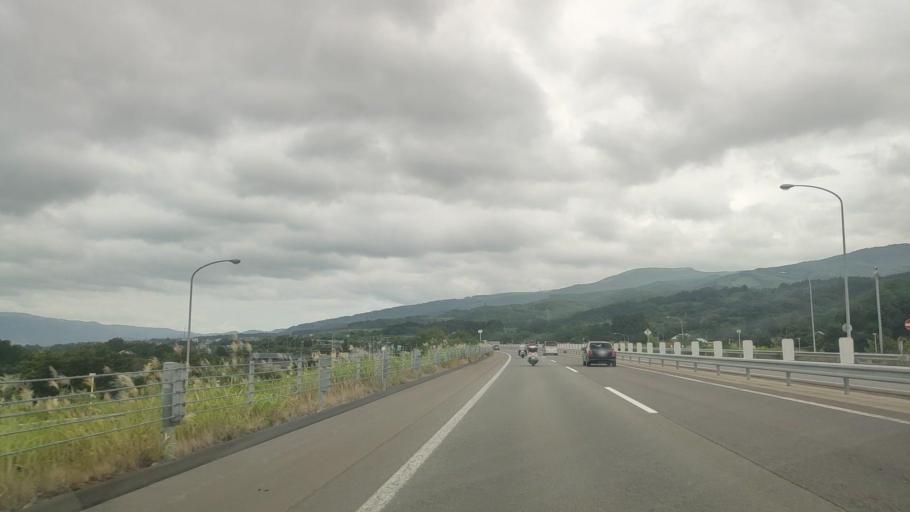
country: JP
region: Hokkaido
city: Nanae
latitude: 41.8671
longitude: 140.7300
